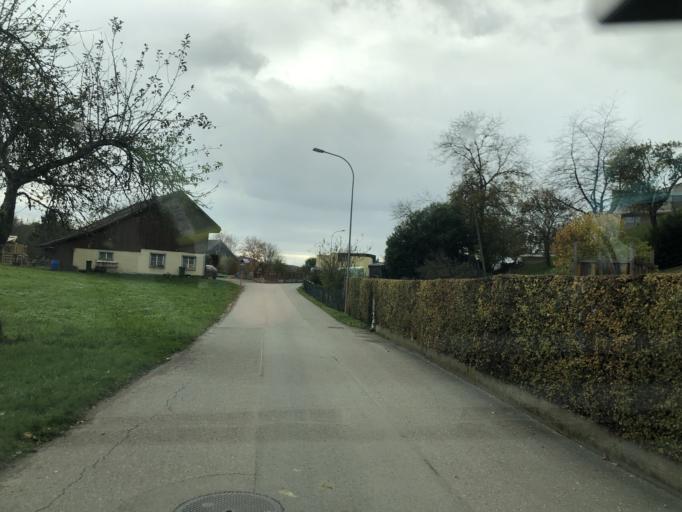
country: CH
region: Aargau
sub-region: Bezirk Baden
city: Neuenhof
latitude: 47.4690
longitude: 8.3424
